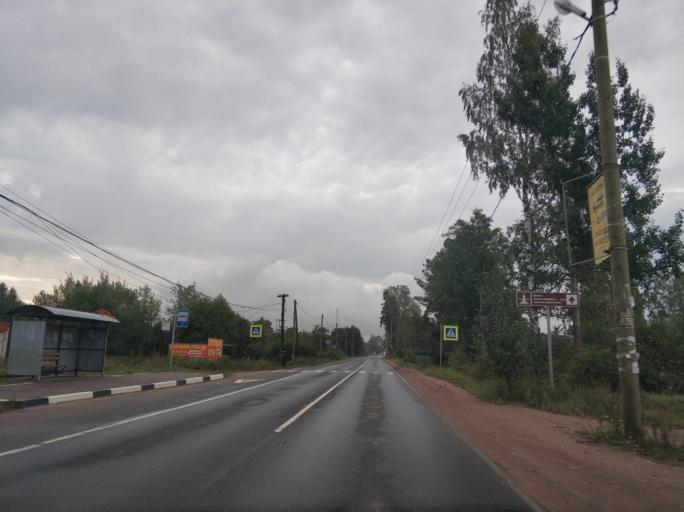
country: RU
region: Leningrad
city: Borisova Griva
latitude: 60.0849
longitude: 30.8878
